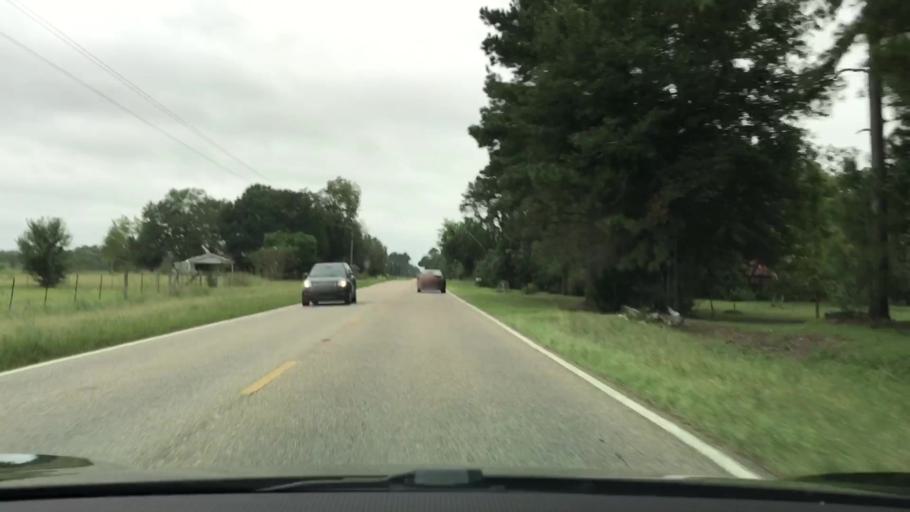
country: US
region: Alabama
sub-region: Geneva County
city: Samson
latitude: 31.1624
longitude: -86.1420
